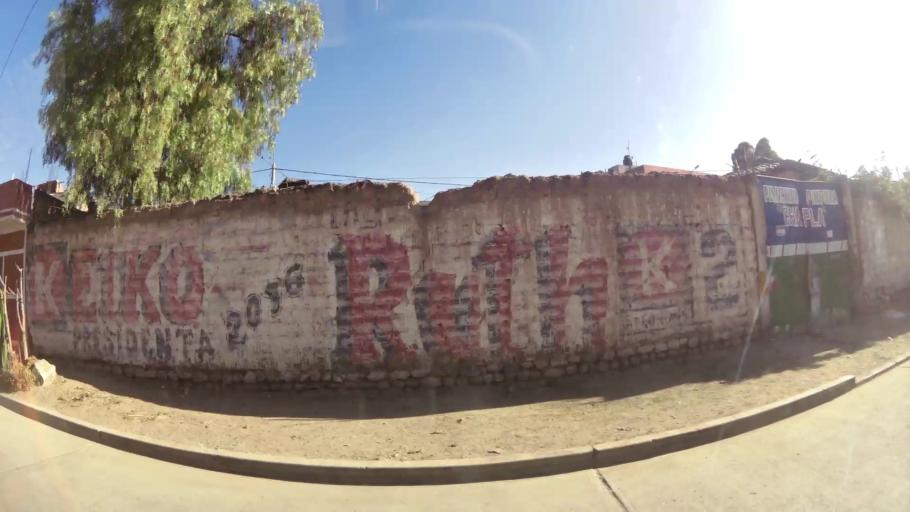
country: PE
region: Ayacucho
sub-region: Provincia de Huamanga
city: Ayacucho
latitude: -13.1556
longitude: -74.2158
